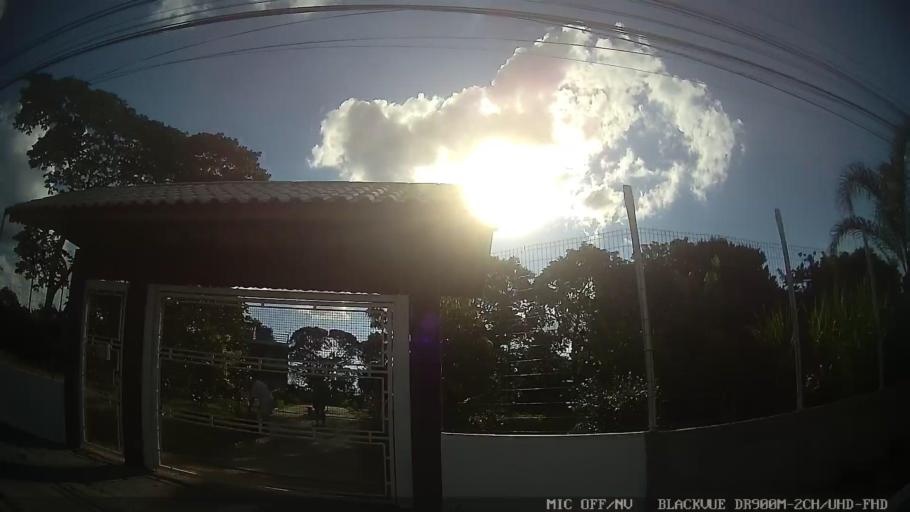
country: BR
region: Minas Gerais
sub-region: Extrema
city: Extrema
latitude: -22.8473
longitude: -46.3290
